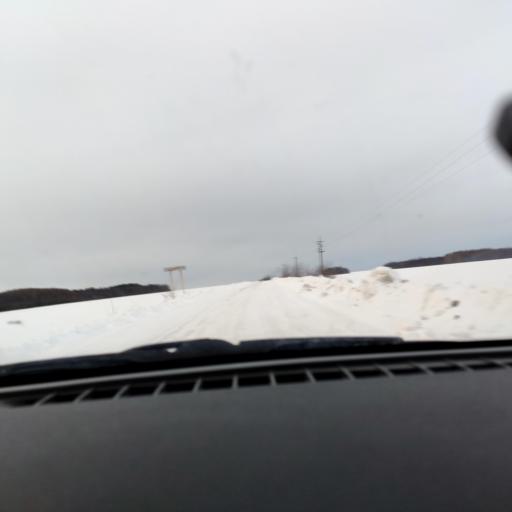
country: RU
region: Bashkortostan
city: Iglino
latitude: 54.7403
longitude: 56.5379
